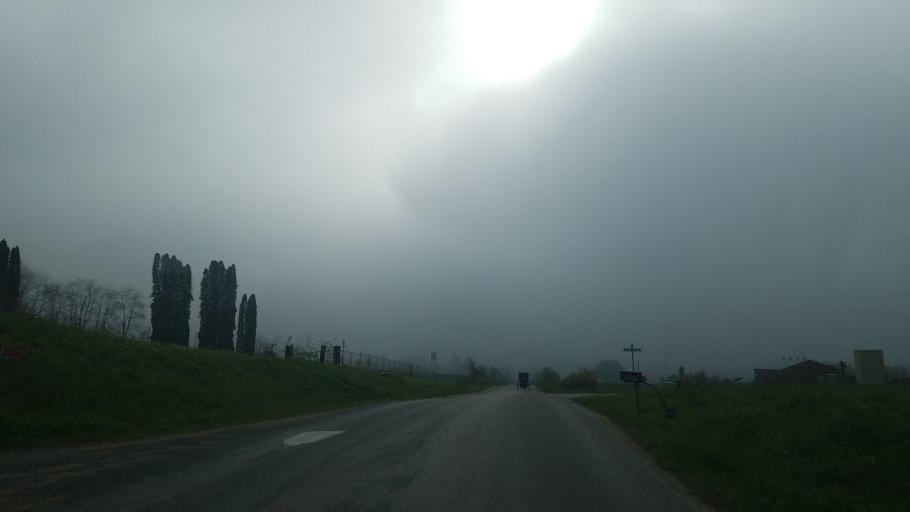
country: US
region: Wisconsin
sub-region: Vernon County
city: Hillsboro
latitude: 43.6187
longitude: -90.3926
